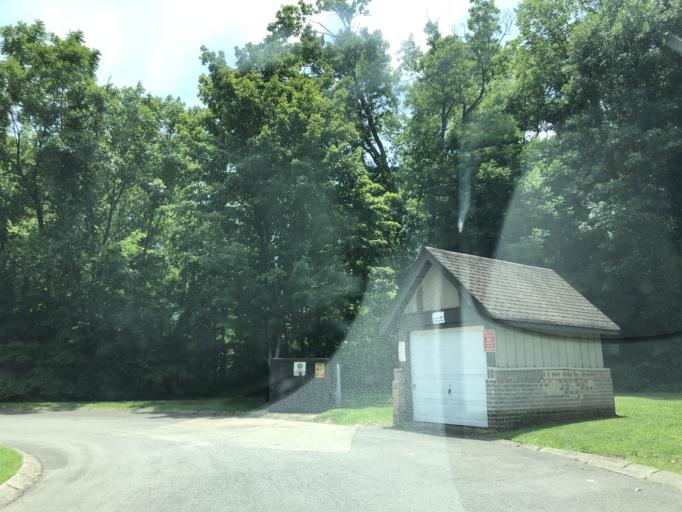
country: US
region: Tennessee
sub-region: Rutherford County
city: La Vergne
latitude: 36.0422
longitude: -86.6644
